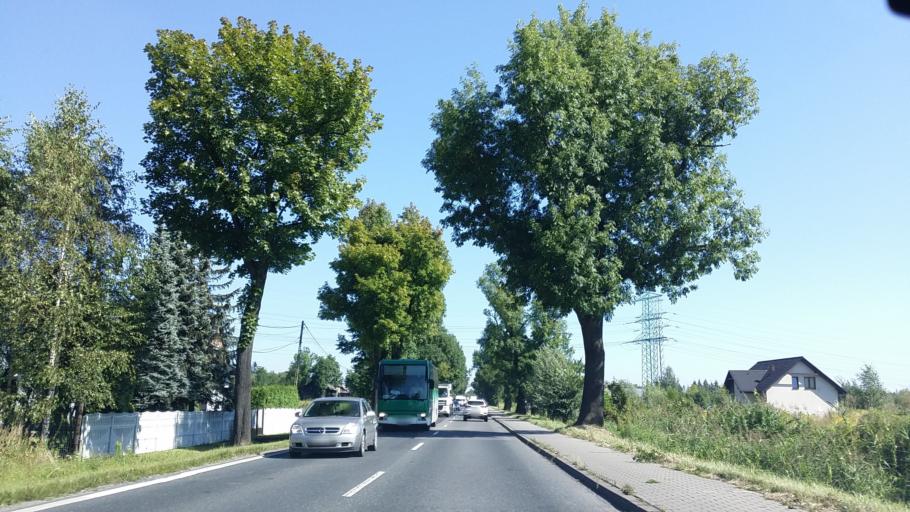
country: PL
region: Lesser Poland Voivodeship
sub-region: Powiat oswiecimski
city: Babice
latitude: 50.0815
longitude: 19.1958
